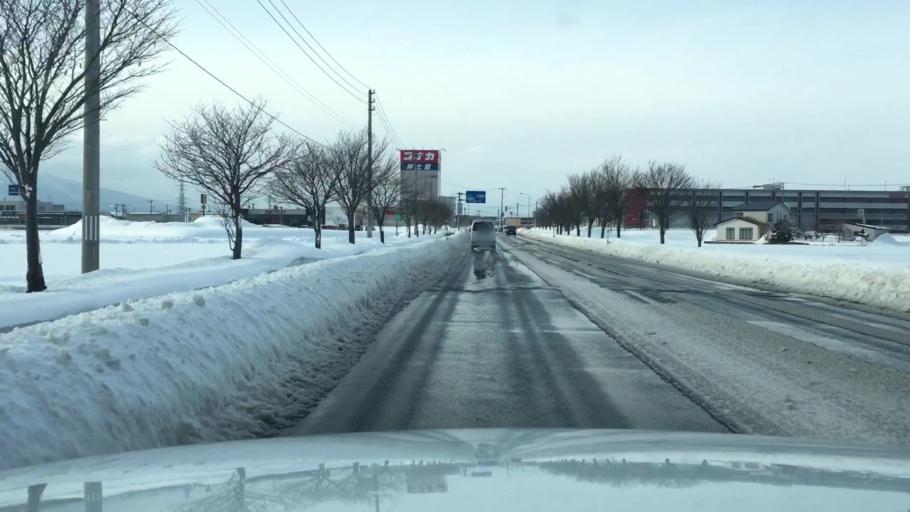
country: JP
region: Aomori
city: Hirosaki
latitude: 40.5972
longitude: 140.5157
